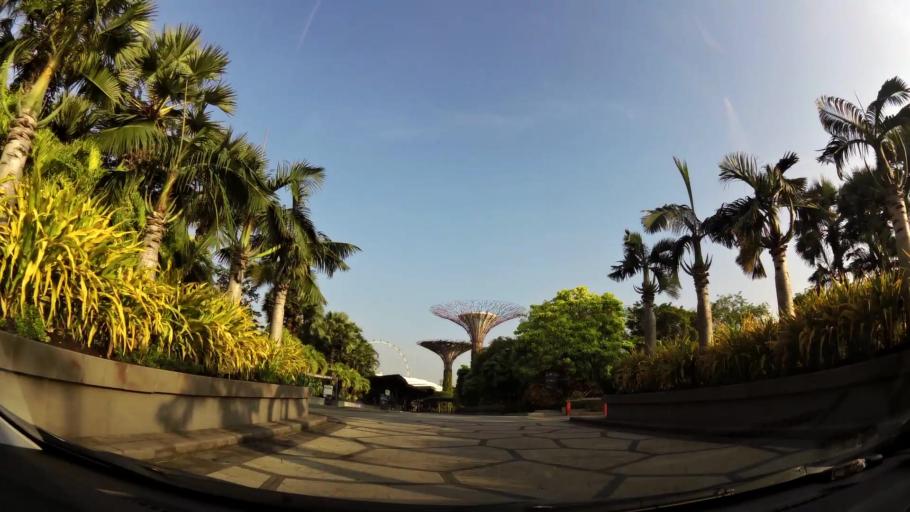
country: SG
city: Singapore
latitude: 1.2808
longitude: 103.8659
